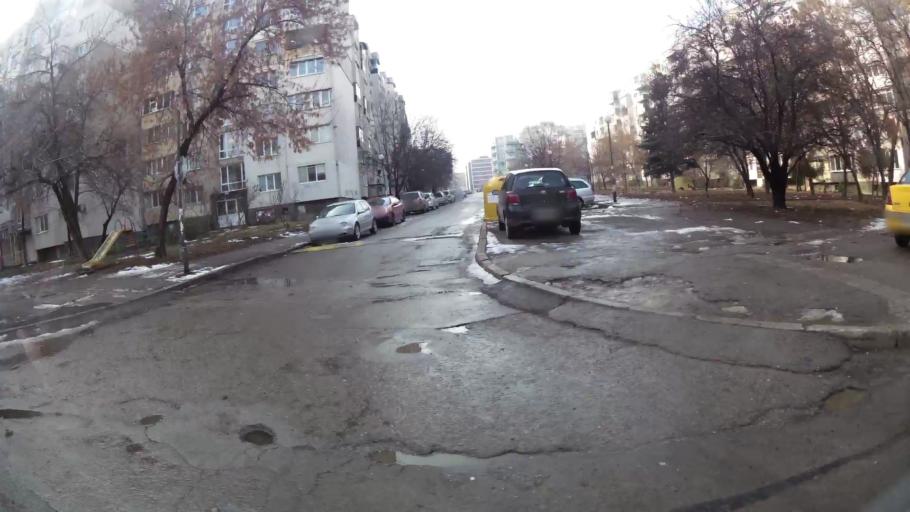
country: BG
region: Sofia-Capital
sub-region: Stolichna Obshtina
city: Sofia
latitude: 42.7181
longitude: 23.2650
